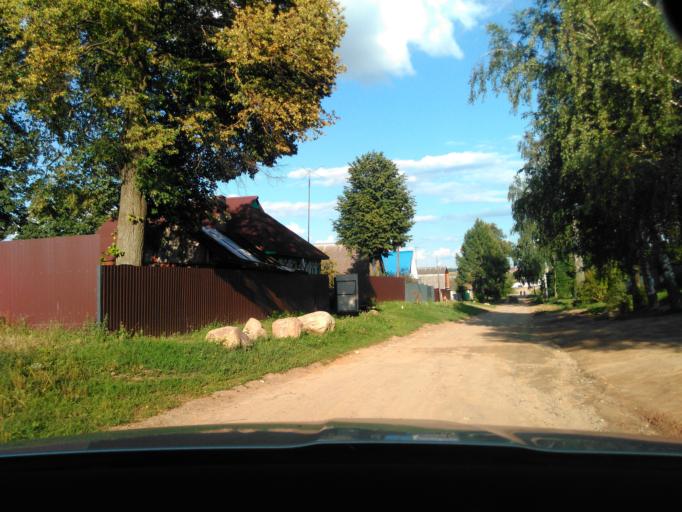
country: RU
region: Tverskaya
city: Zavidovo
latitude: 56.5814
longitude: 36.5158
